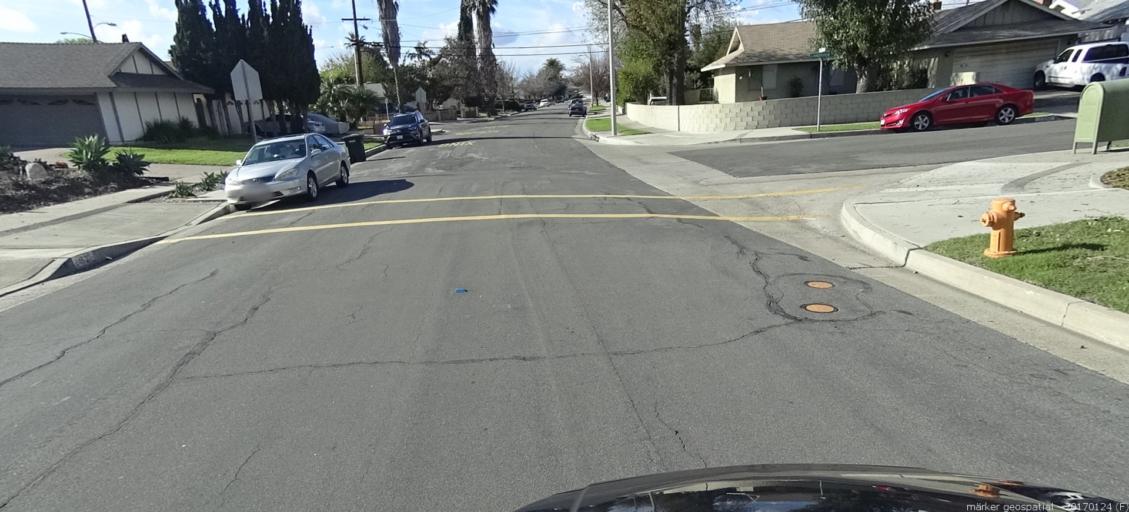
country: US
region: California
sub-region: Orange County
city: Laguna Hills
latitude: 33.6145
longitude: -117.6993
